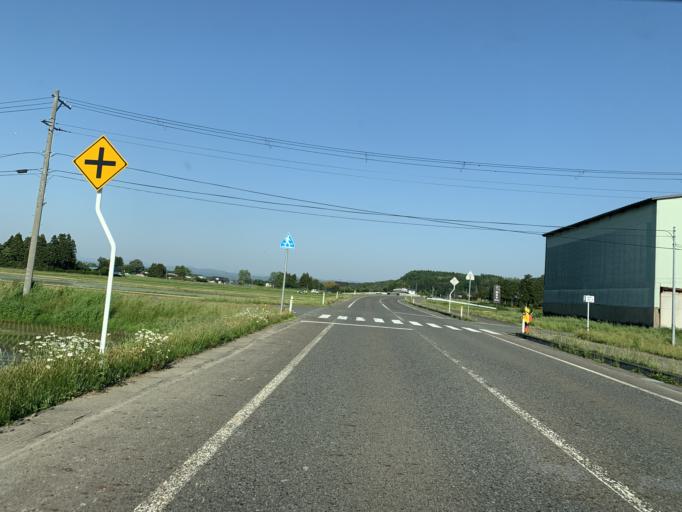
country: JP
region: Iwate
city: Kitakami
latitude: 39.2844
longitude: 141.0154
